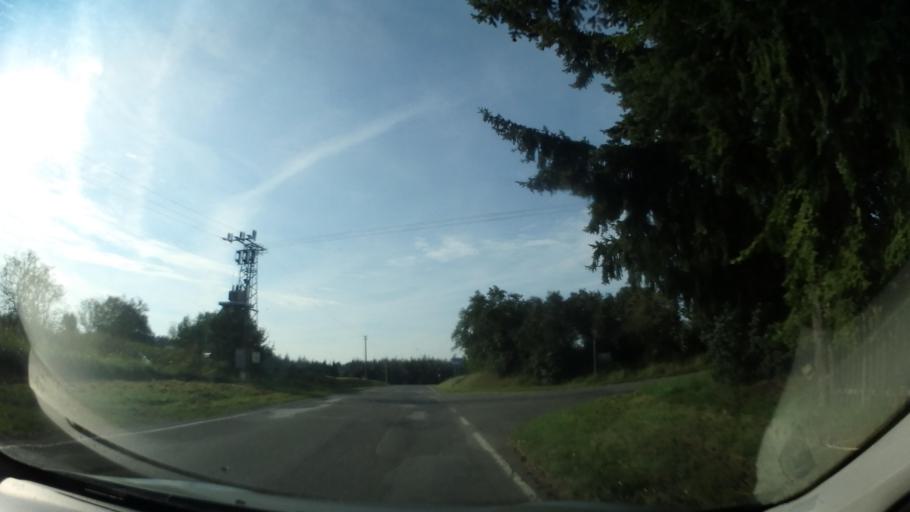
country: CZ
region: Jihocesky
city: Cimelice
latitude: 49.4378
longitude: 14.1442
